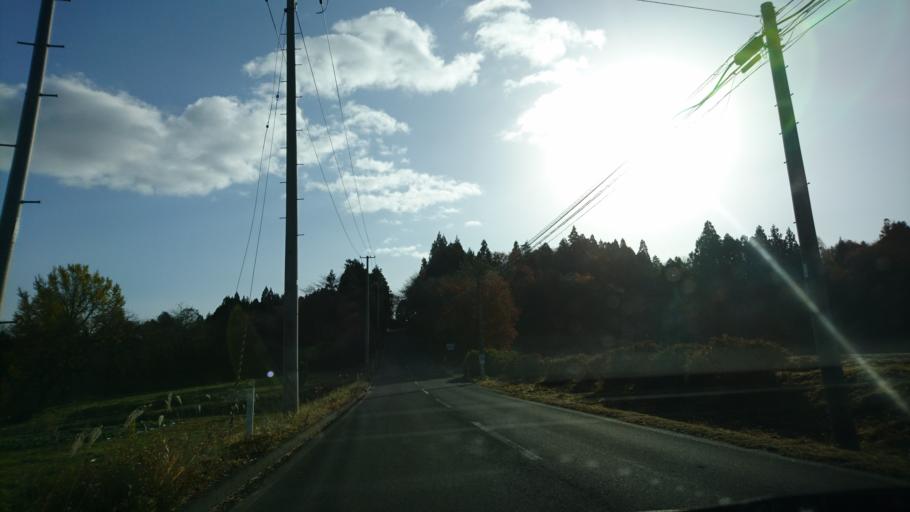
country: JP
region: Iwate
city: Ichinoseki
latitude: 38.8872
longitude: 141.2892
